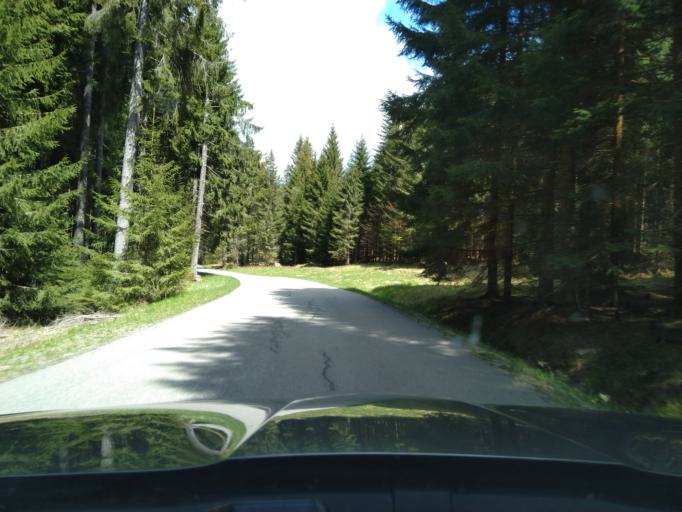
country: CZ
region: Jihocesky
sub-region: Okres Prachatice
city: Borova Lada
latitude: 49.0083
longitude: 13.7094
